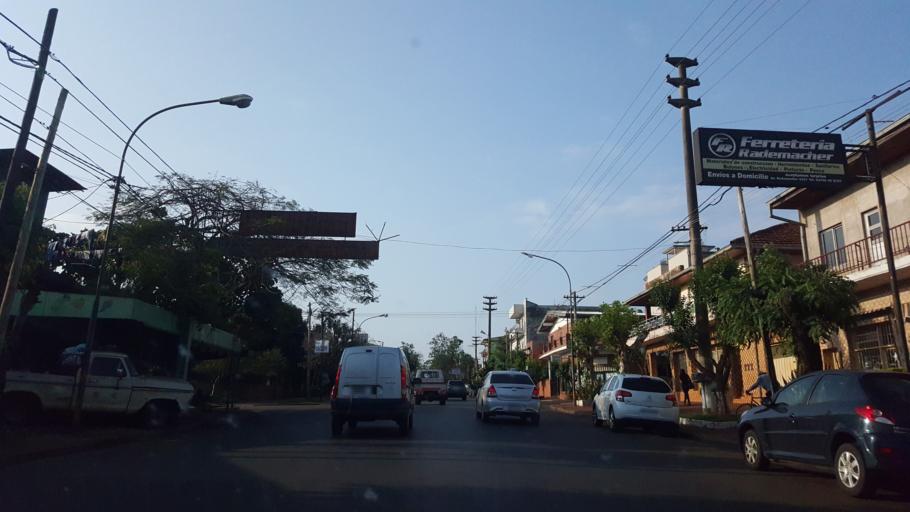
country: AR
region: Misiones
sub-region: Departamento de Capital
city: Posadas
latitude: -27.3894
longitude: -55.8968
